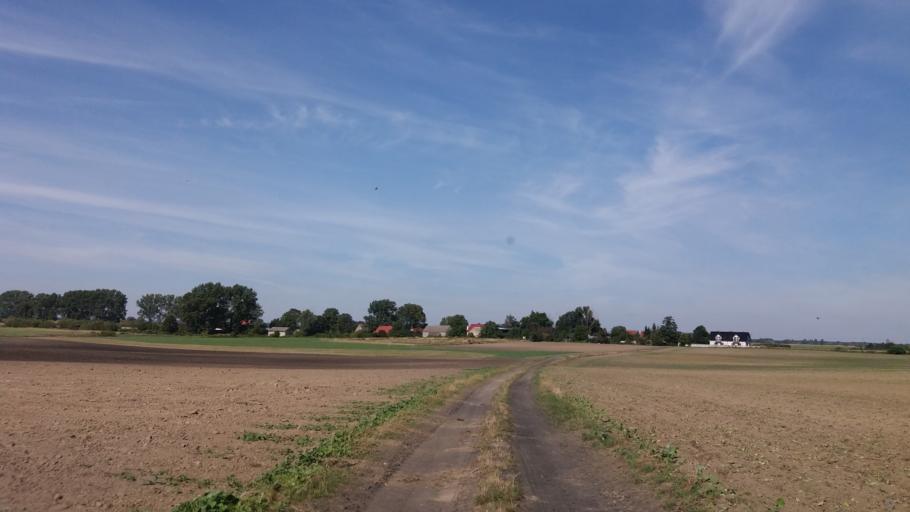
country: PL
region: West Pomeranian Voivodeship
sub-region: Powiat choszczenski
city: Choszczno
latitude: 53.1251
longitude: 15.4114
